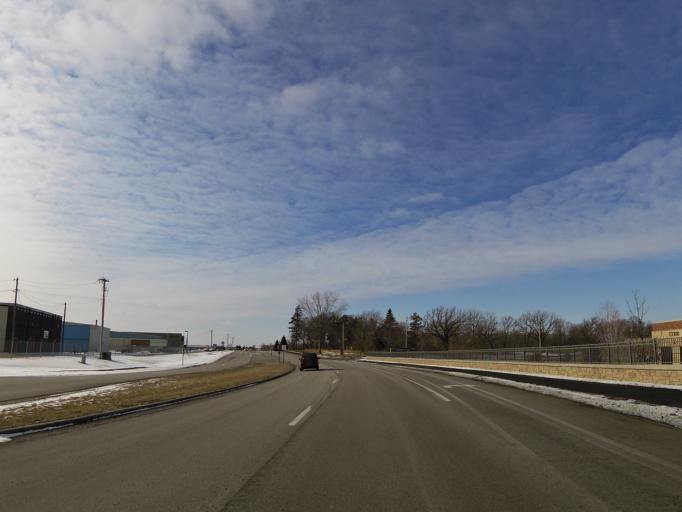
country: US
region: Minnesota
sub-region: Hennepin County
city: Eden Prairie
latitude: 44.8288
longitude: -93.4464
